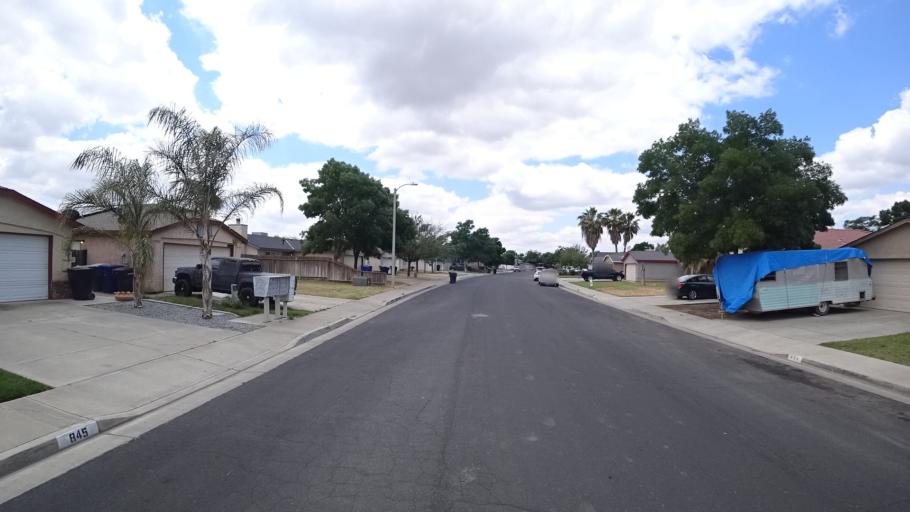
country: US
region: California
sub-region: Kings County
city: Hanford
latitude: 36.3098
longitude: -119.6566
